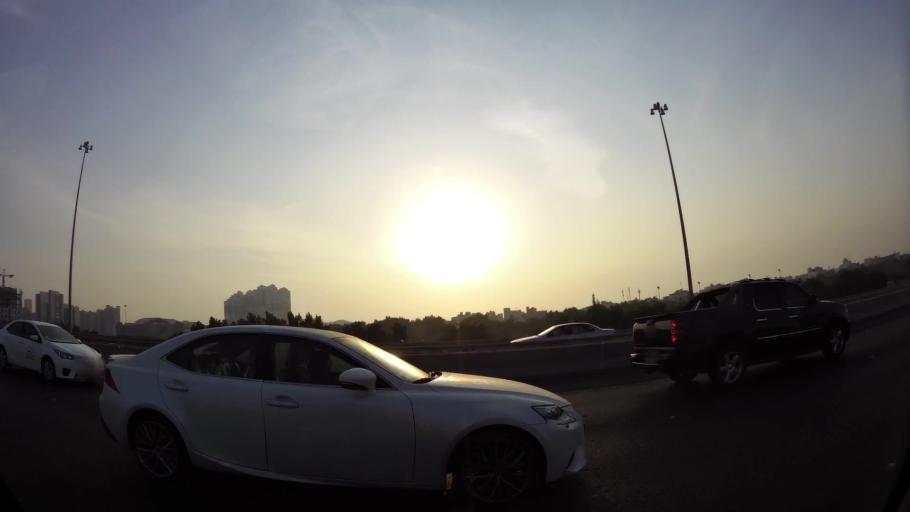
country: KW
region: Muhafazat Hawalli
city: Salwa
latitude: 29.2713
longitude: 48.0840
